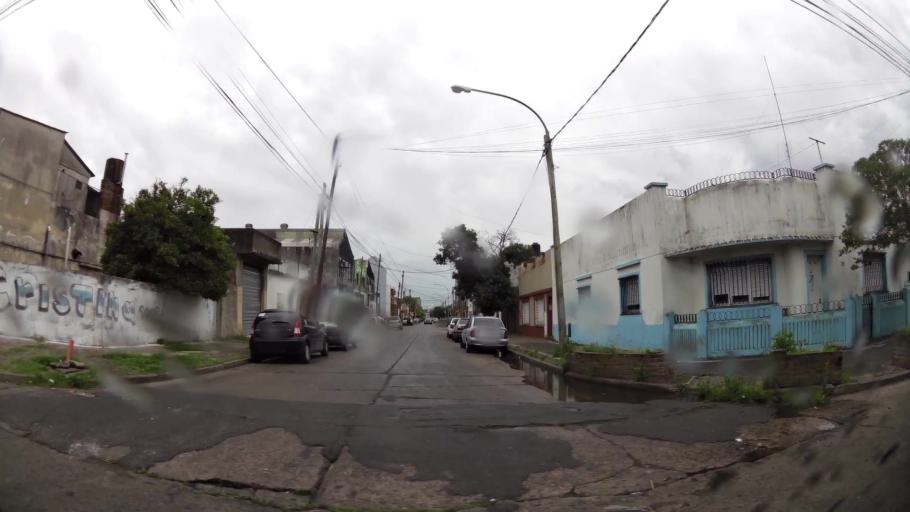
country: AR
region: Buenos Aires
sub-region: Partido de Lanus
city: Lanus
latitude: -34.6881
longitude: -58.4022
